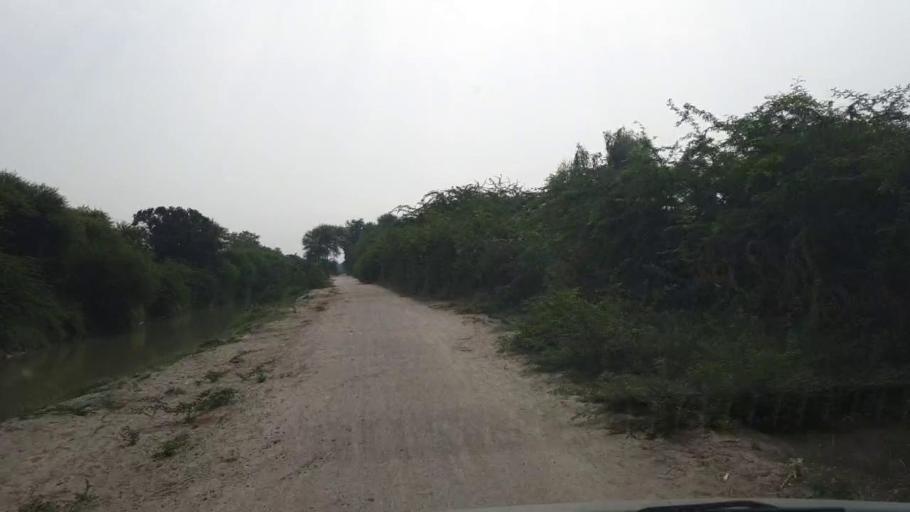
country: PK
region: Sindh
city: Matli
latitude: 25.0046
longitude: 68.7011
